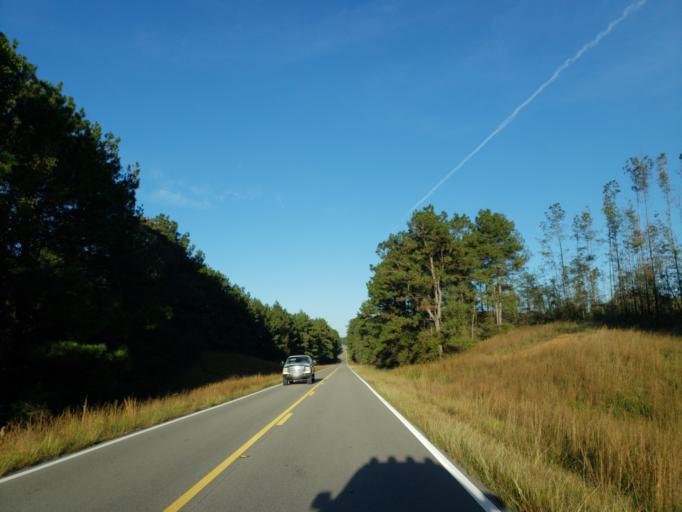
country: US
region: Mississippi
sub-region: Perry County
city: Richton
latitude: 31.3581
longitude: -88.7376
